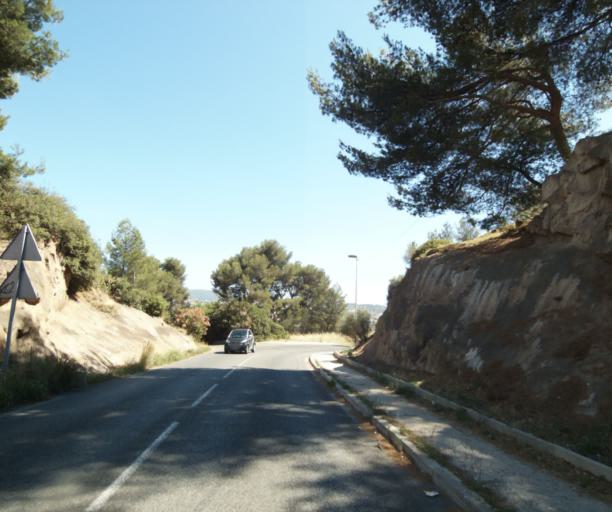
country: FR
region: Provence-Alpes-Cote d'Azur
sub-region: Departement du Var
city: La Garde
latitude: 43.1341
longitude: 6.0092
